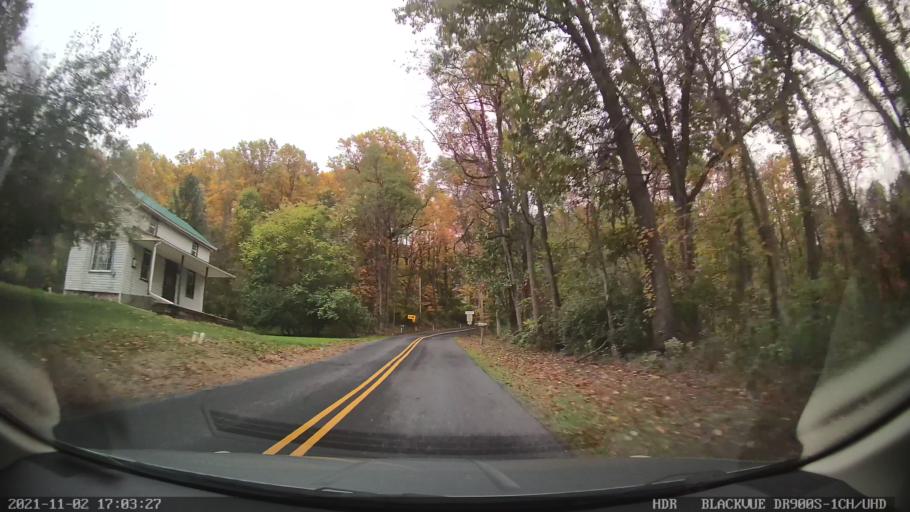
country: US
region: Pennsylvania
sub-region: Berks County
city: Fleetwood
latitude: 40.4427
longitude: -75.8417
